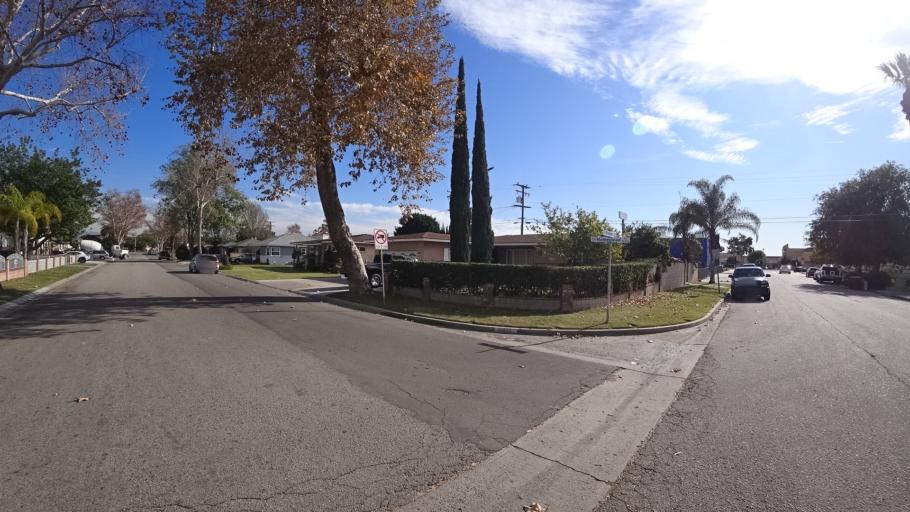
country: US
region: California
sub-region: Orange County
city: Garden Grove
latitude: 33.7755
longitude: -117.9213
